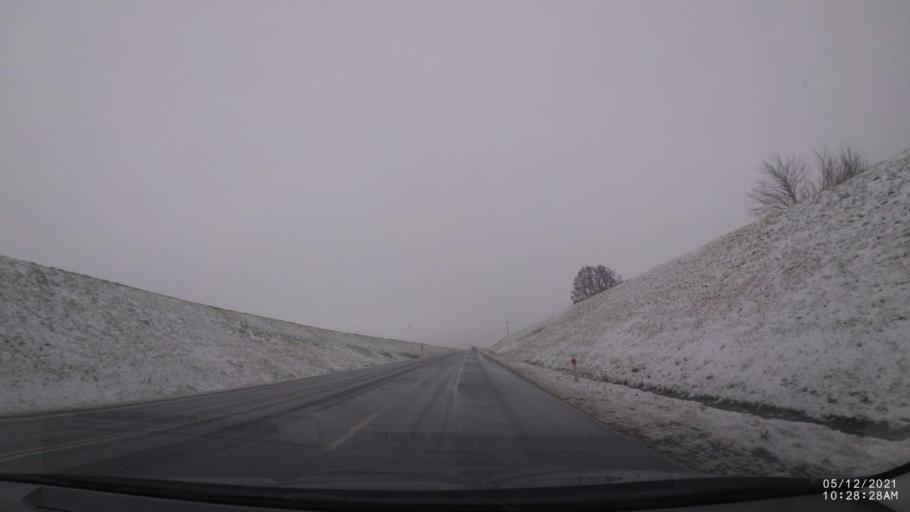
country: CZ
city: Vamberk
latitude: 50.1228
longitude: 16.2834
